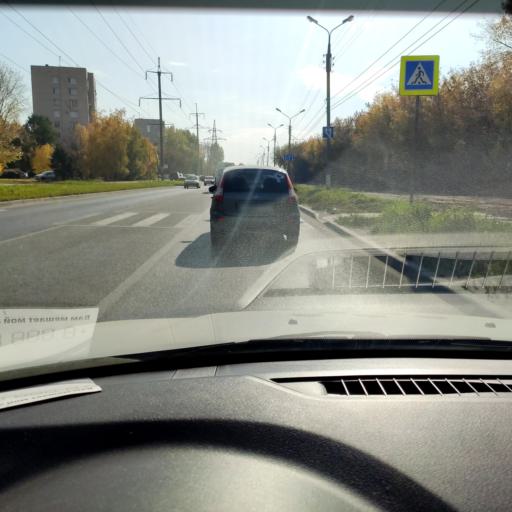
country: RU
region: Samara
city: Tol'yatti
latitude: 53.5275
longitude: 49.3963
